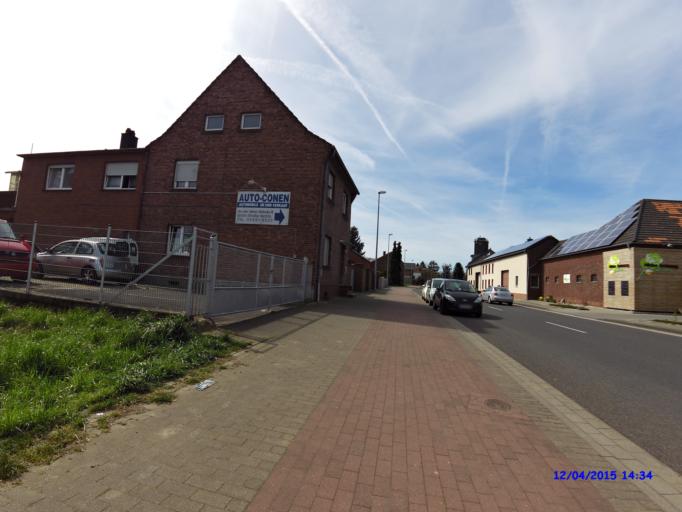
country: DE
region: North Rhine-Westphalia
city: Geilenkirchen
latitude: 50.9667
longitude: 6.1074
